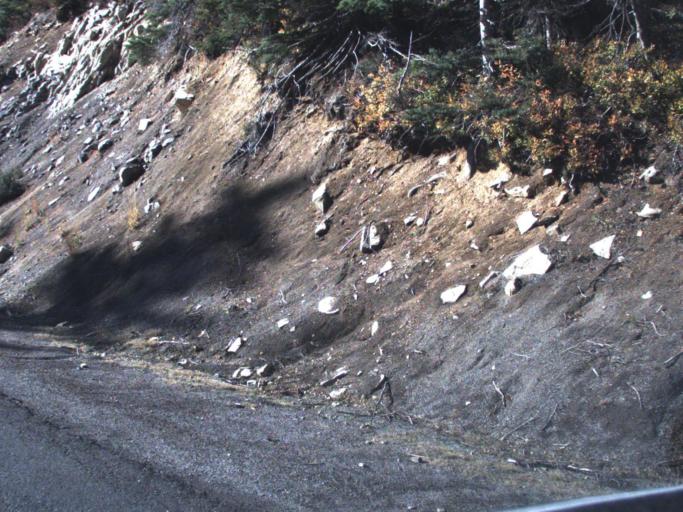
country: US
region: Washington
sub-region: Yakima County
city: Tieton
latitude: 46.6449
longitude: -121.3773
